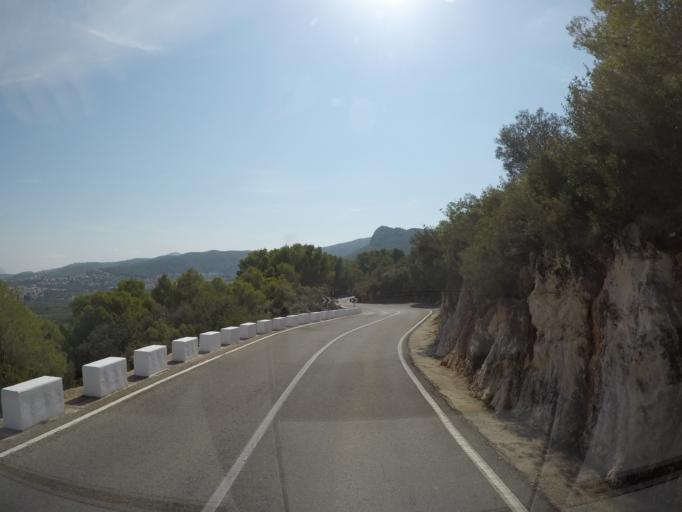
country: ES
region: Valencia
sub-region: Provincia de Alicante
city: Tormos
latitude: 38.7850
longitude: -0.0824
